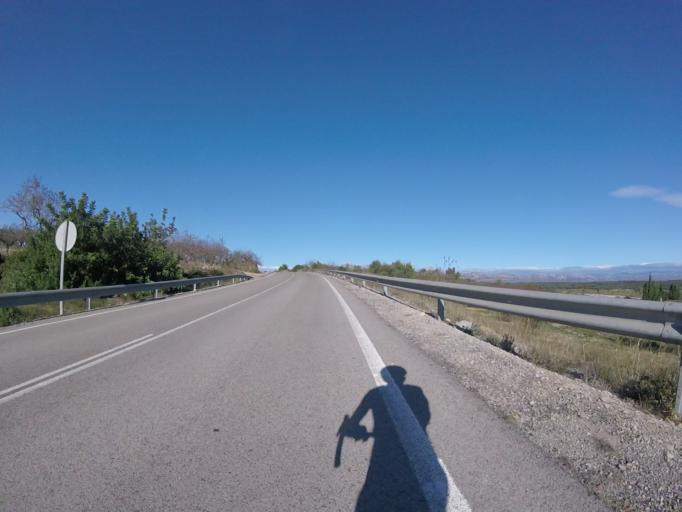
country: ES
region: Valencia
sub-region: Provincia de Castello
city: Cervera del Maestre
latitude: 40.4721
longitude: 0.2398
